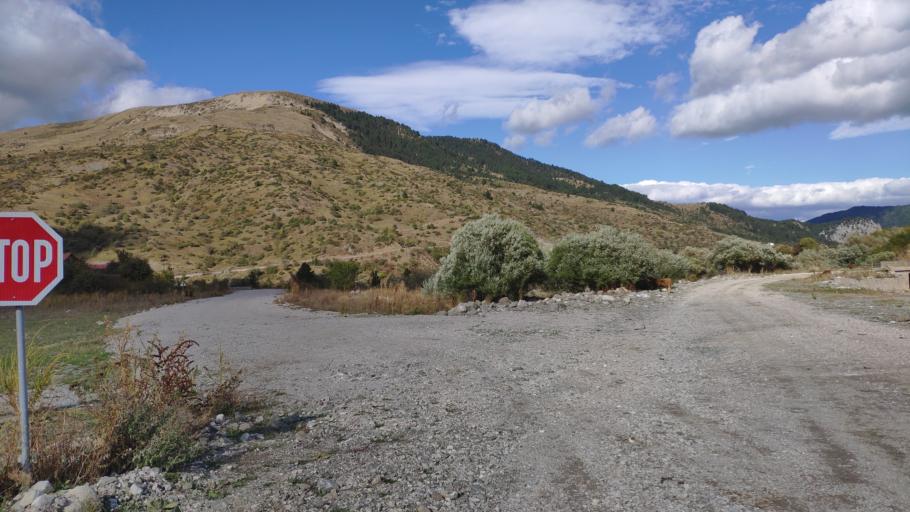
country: AL
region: Korce
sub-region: Rrethi i Devollit
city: Miras
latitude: 40.3920
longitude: 20.8369
